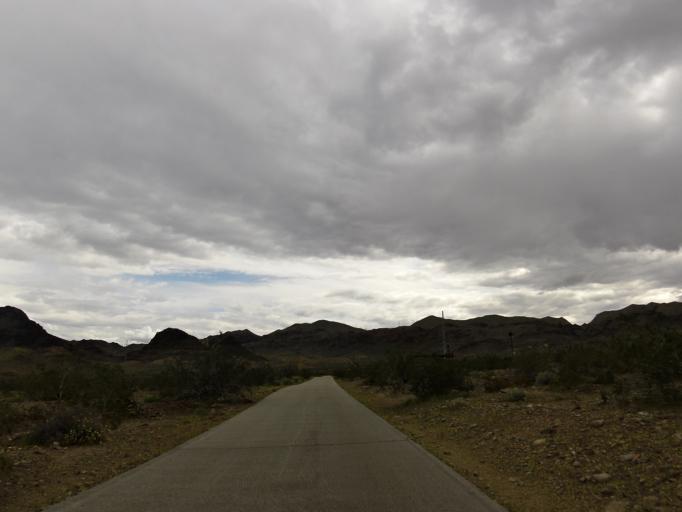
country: US
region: Nevada
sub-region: Clark County
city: Boulder City
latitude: 36.0226
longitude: -114.7965
